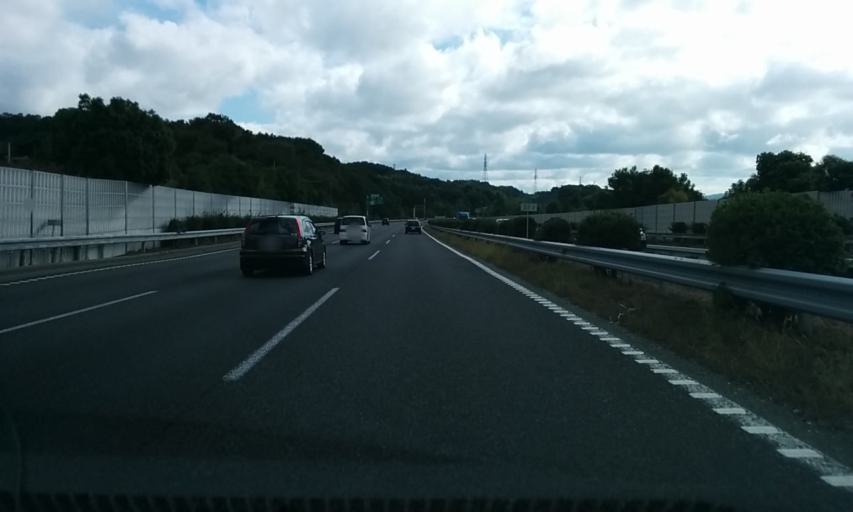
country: JP
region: Hyogo
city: Sandacho
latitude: 34.8841
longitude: 135.1777
